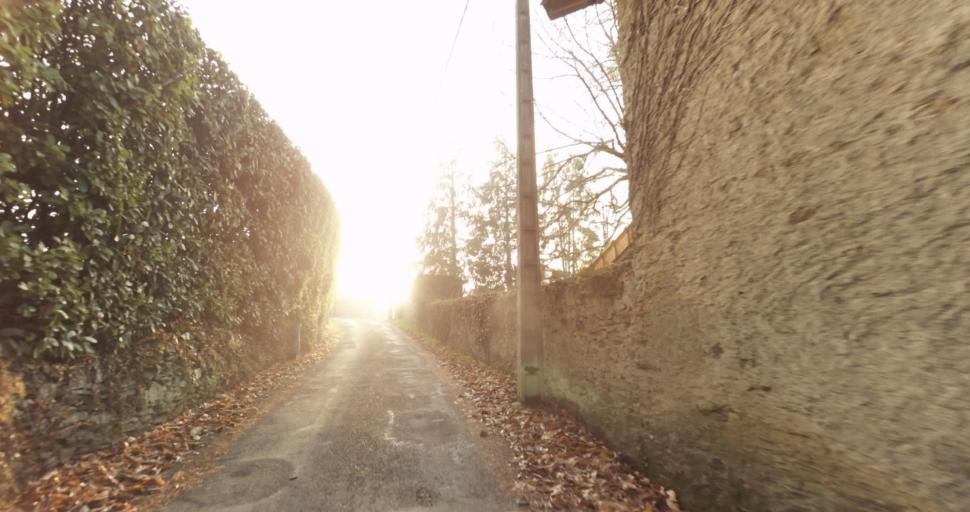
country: FR
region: Limousin
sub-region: Departement de la Haute-Vienne
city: Aixe-sur-Vienne
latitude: 45.7947
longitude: 1.1526
